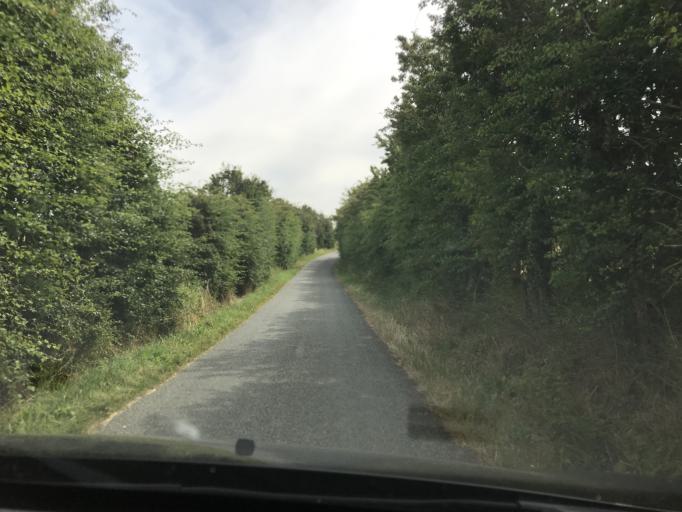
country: DK
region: South Denmark
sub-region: AEro Kommune
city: AEroskobing
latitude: 54.9224
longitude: 10.2456
